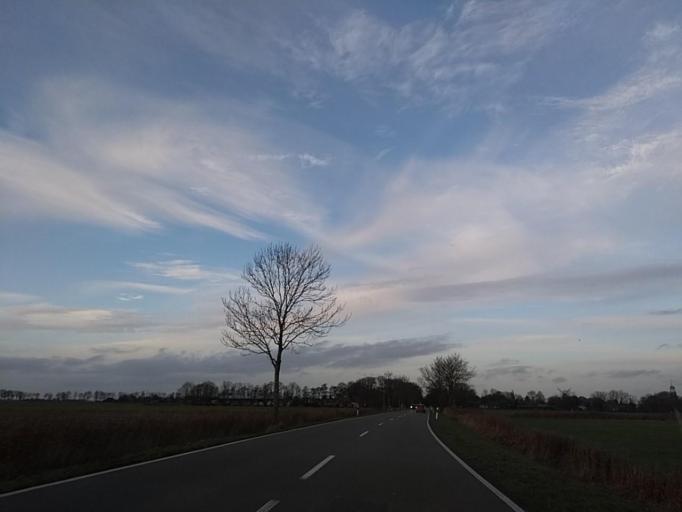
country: DE
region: Lower Saxony
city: Jemgum
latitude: 53.2578
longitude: 7.3852
